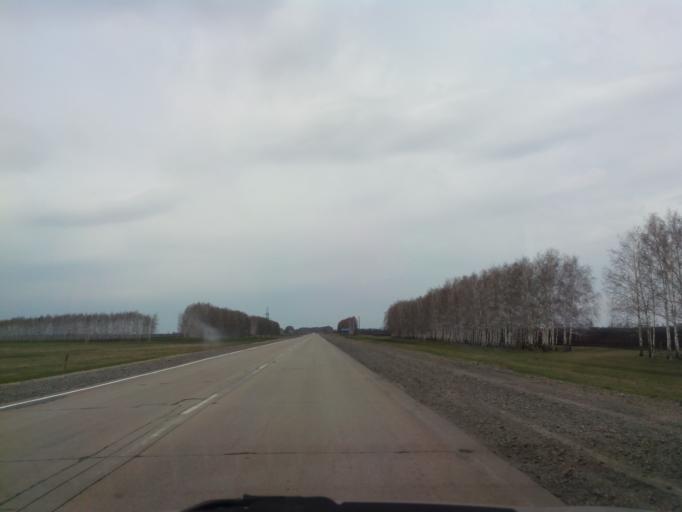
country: RU
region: Tambov
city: Satinka
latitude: 52.2346
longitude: 41.5370
